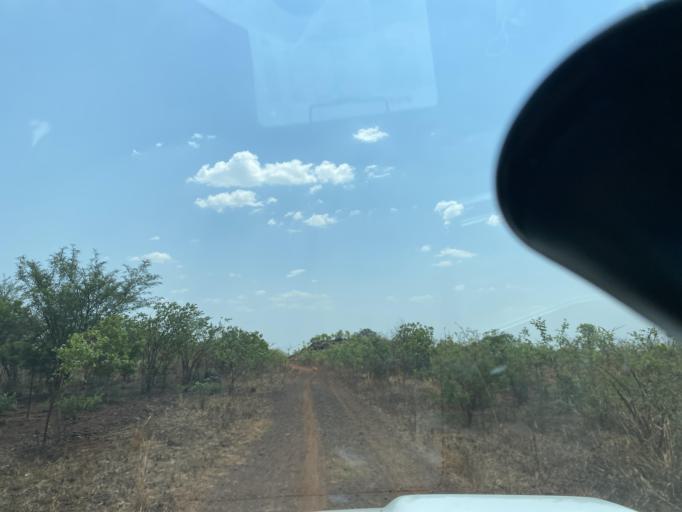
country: ZM
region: Lusaka
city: Lusaka
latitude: -15.4977
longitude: 27.9648
